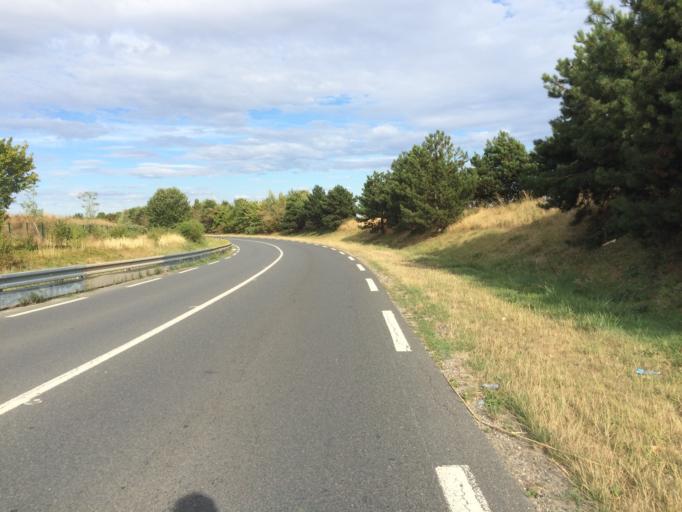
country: FR
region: Ile-de-France
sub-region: Departement de l'Essonne
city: Chilly-Mazarin
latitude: 48.7129
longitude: 2.3148
